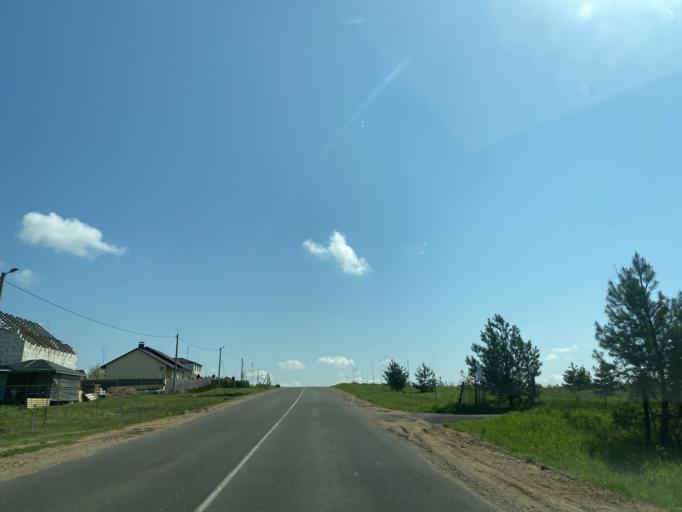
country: BY
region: Minsk
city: Horad Barysaw
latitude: 54.1784
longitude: 28.5462
